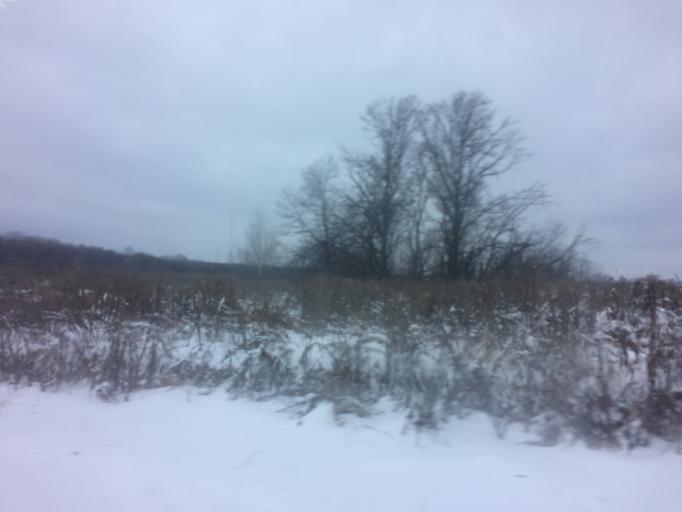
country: RU
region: Tula
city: Mendeleyevskiy
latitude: 54.1395
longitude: 37.6363
